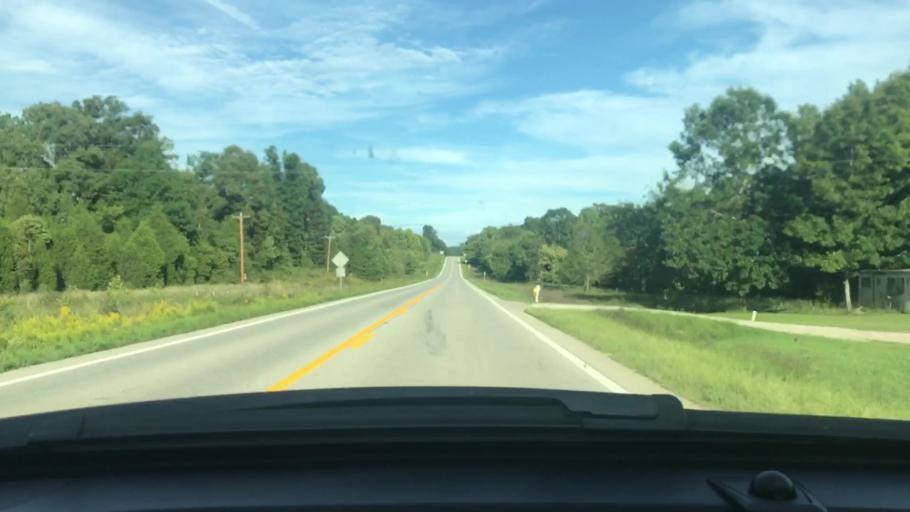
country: US
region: Arkansas
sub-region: Sharp County
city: Cherokee Village
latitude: 36.2746
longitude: -91.3486
